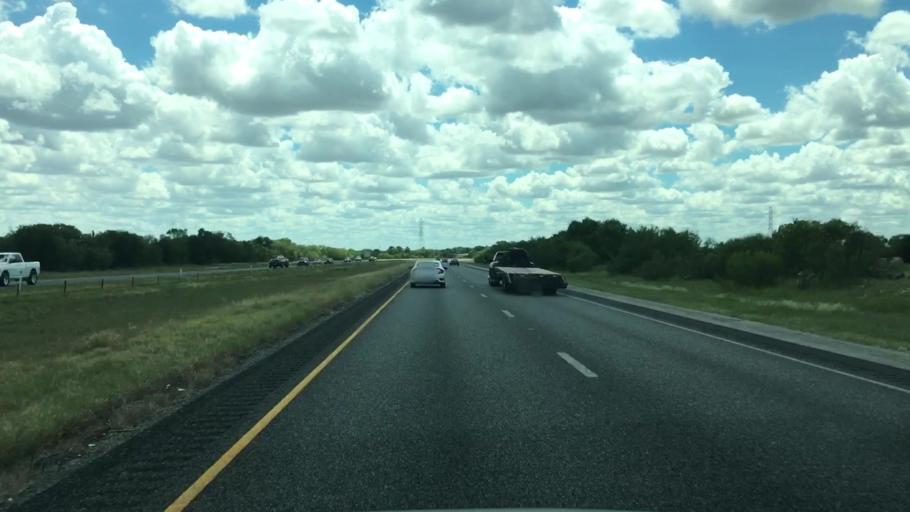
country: US
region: Texas
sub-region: Bexar County
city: Elmendorf
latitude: 29.2569
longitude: -98.3953
